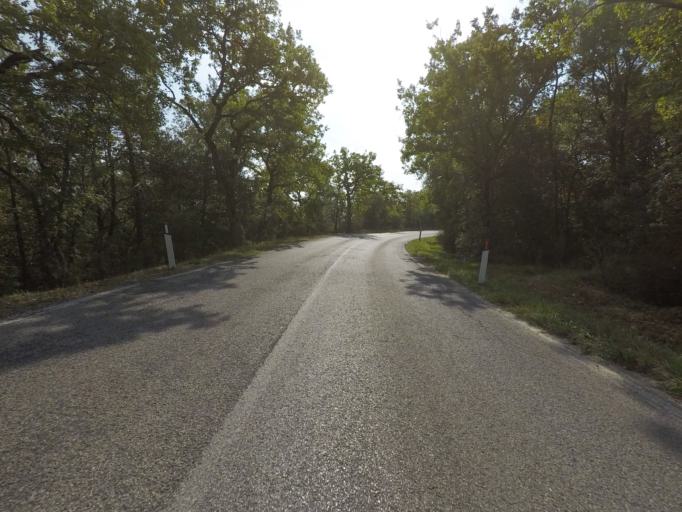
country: IT
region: Tuscany
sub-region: Provincia di Siena
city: Belverde
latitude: 43.4065
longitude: 11.3521
